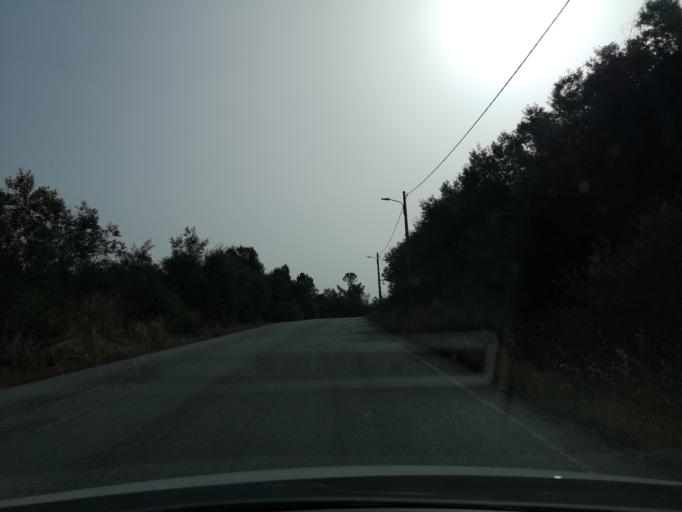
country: PT
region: Castelo Branco
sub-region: Belmonte
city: Belmonte
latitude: 40.3738
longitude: -7.3250
